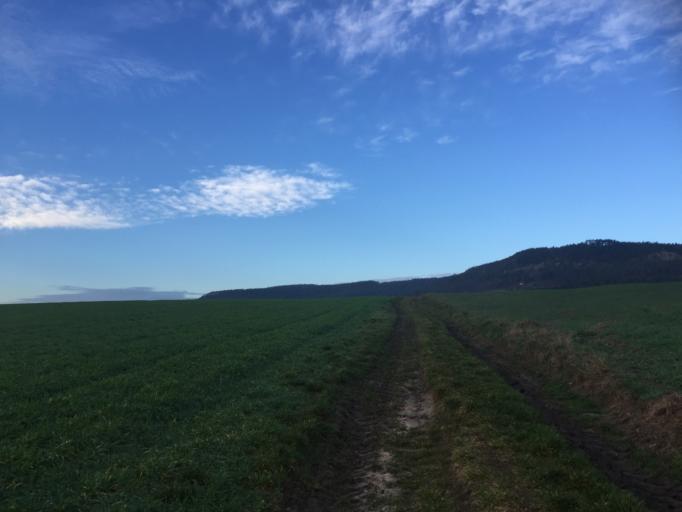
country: DE
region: Thuringia
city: Orlamunde
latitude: 50.7664
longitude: 11.4956
